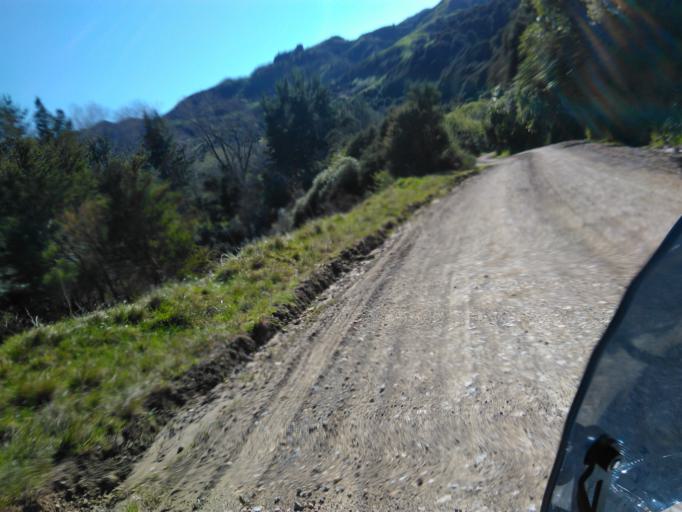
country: NZ
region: Gisborne
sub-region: Gisborne District
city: Gisborne
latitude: -38.3907
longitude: 177.6617
